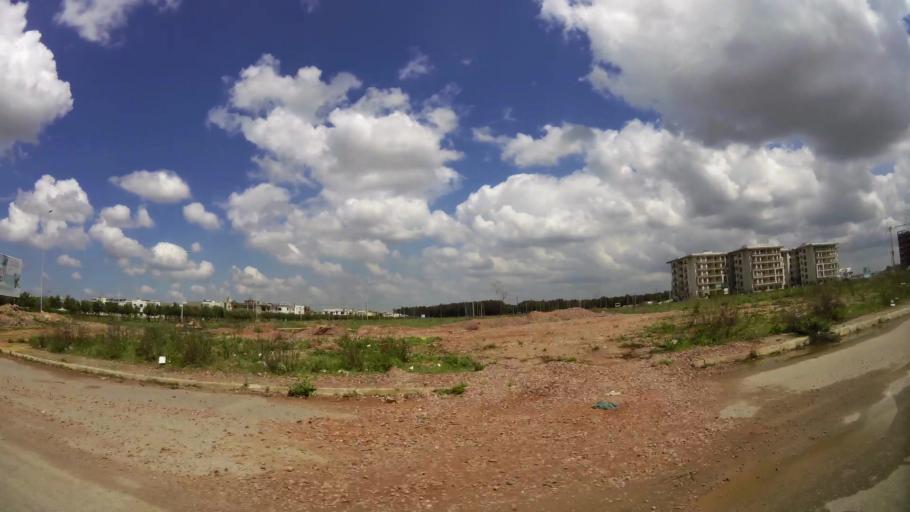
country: MA
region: Chaouia-Ouardigha
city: Nouaseur
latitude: 33.3931
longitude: -7.5621
